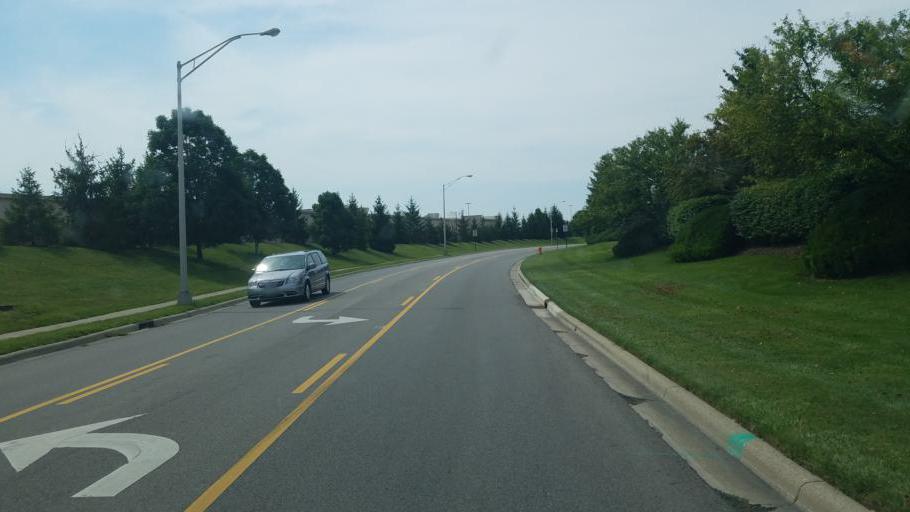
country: US
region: Ohio
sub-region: Franklin County
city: Lincoln Village
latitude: 39.9878
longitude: -83.1552
